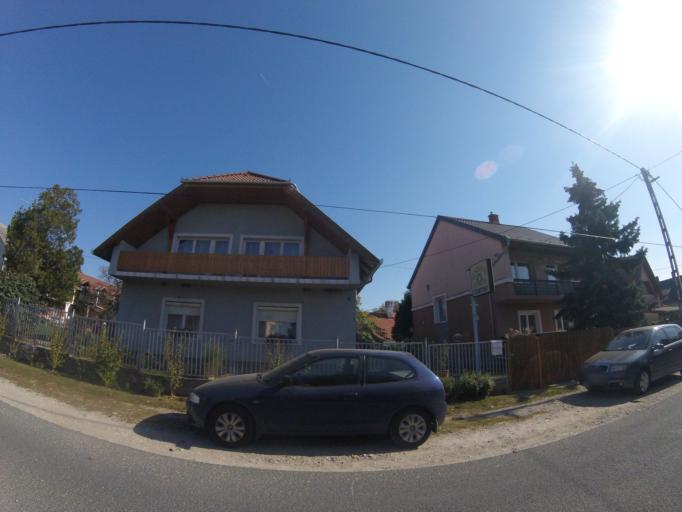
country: HU
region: Zala
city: Gyenesdias
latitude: 46.7752
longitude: 17.2794
